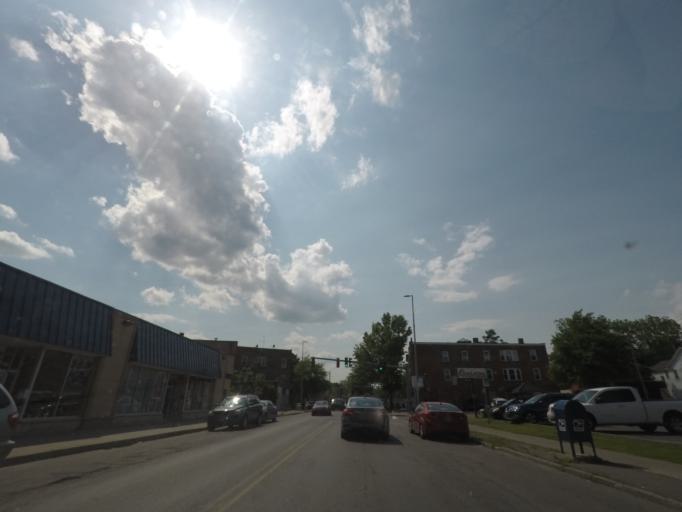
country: US
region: New York
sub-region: Dutchess County
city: Poughkeepsie
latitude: 41.6979
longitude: -73.9105
